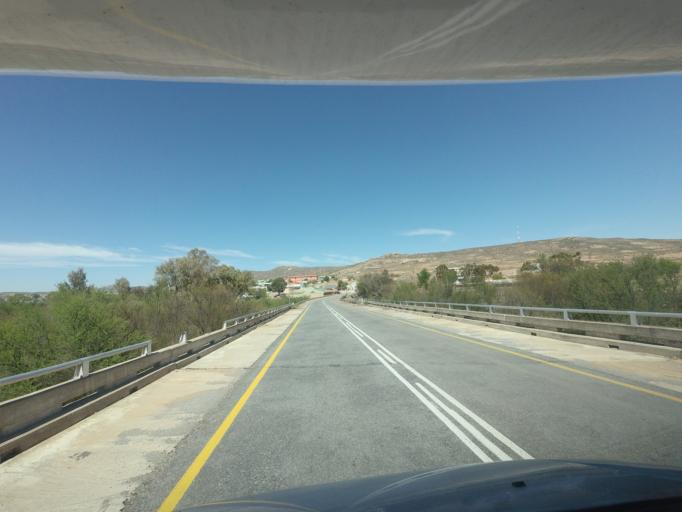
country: ZA
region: Northern Cape
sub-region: Namakwa District Municipality
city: Garies
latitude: -30.5572
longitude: 17.9931
